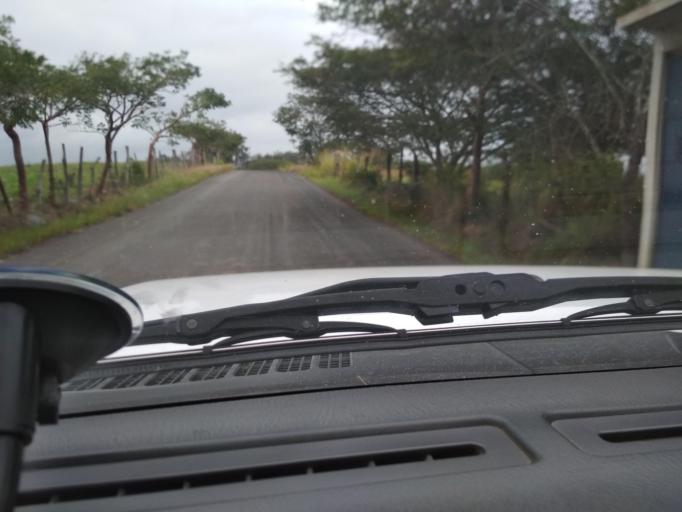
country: MX
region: Veracruz
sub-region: Emiliano Zapata
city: Dos Rios
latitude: 19.5330
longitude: -96.7999
